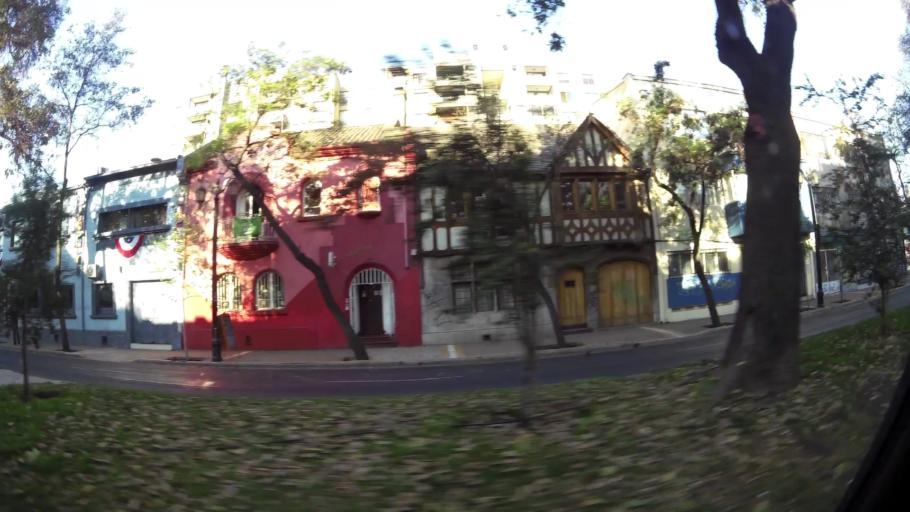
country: CL
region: Santiago Metropolitan
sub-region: Provincia de Santiago
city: Santiago
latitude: -33.4441
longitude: -70.6678
